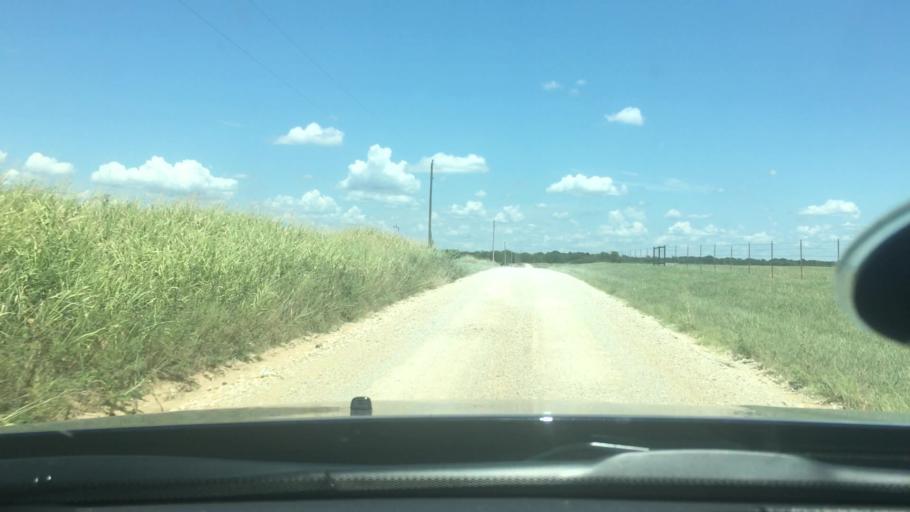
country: US
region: Oklahoma
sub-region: Bryan County
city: Durant
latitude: 34.0016
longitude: -96.1123
